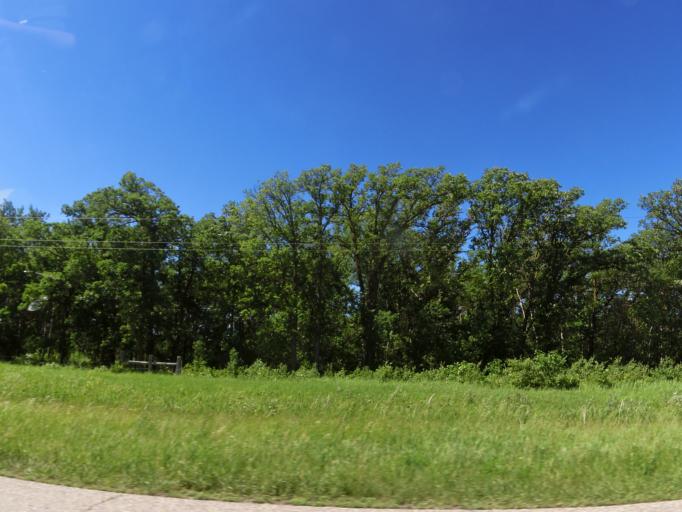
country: US
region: Minnesota
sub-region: Red Lake County
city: Red Lake Falls
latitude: 47.7115
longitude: -96.1664
